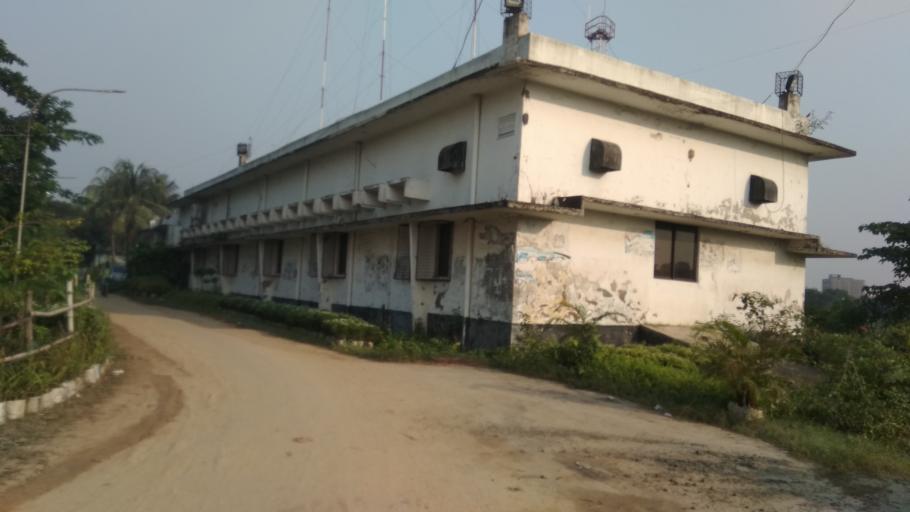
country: BD
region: Dhaka
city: Tungi
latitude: 23.8417
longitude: 90.4198
